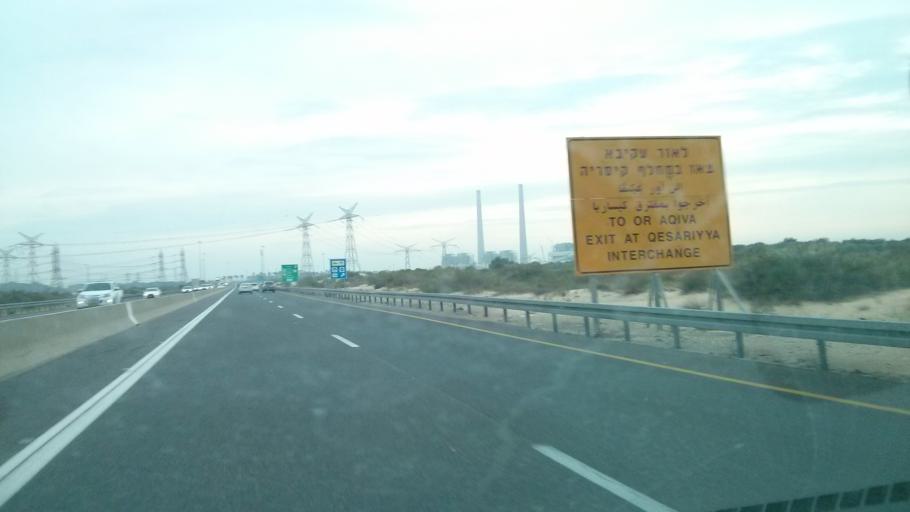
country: IL
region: Haifa
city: Hadera
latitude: 32.4795
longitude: 34.9075
